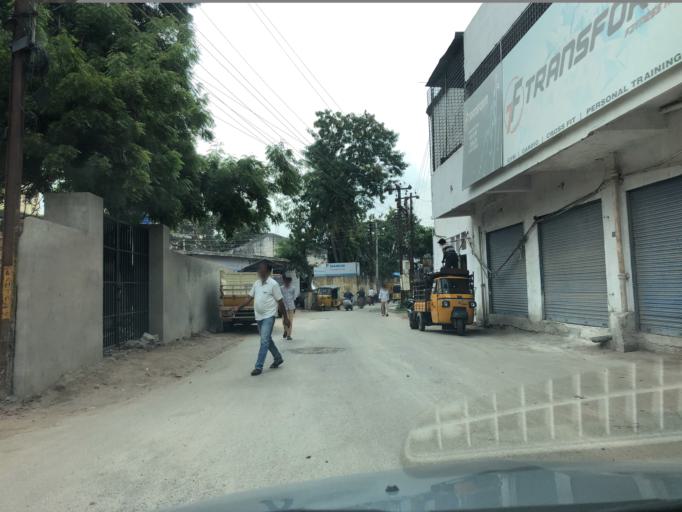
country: IN
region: Telangana
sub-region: Hyderabad
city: Malkajgiri
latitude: 17.4465
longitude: 78.4796
